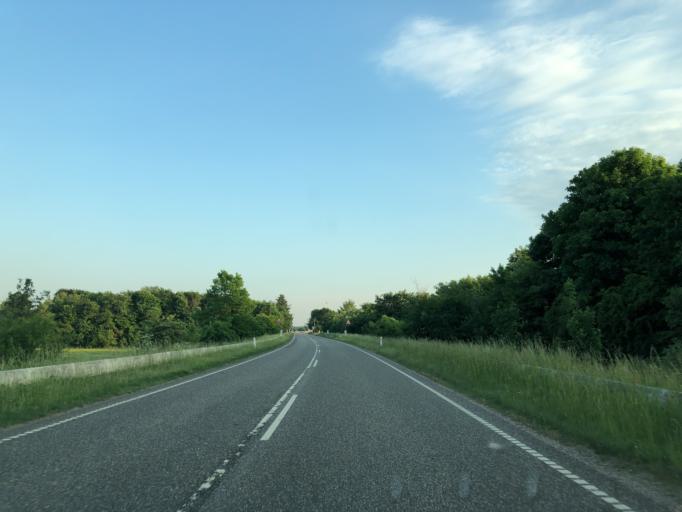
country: DK
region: Central Jutland
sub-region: Holstebro Kommune
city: Ulfborg
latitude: 56.3711
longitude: 8.4407
